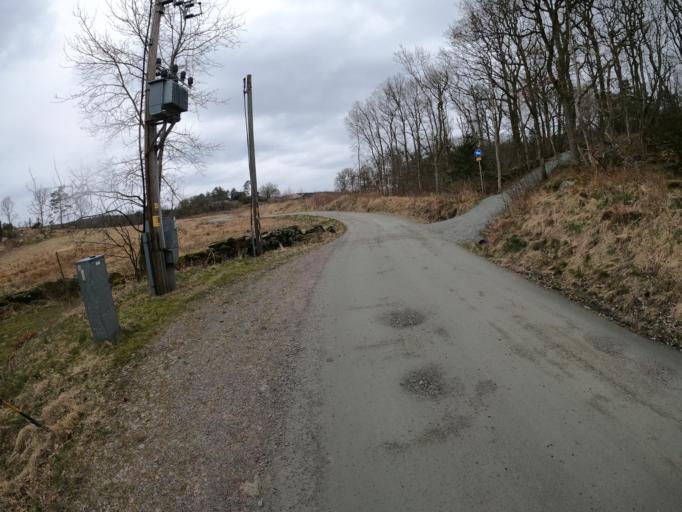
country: SE
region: Vaestra Goetaland
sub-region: Harryda Kommun
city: Molnlycke
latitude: 57.6276
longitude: 12.1081
